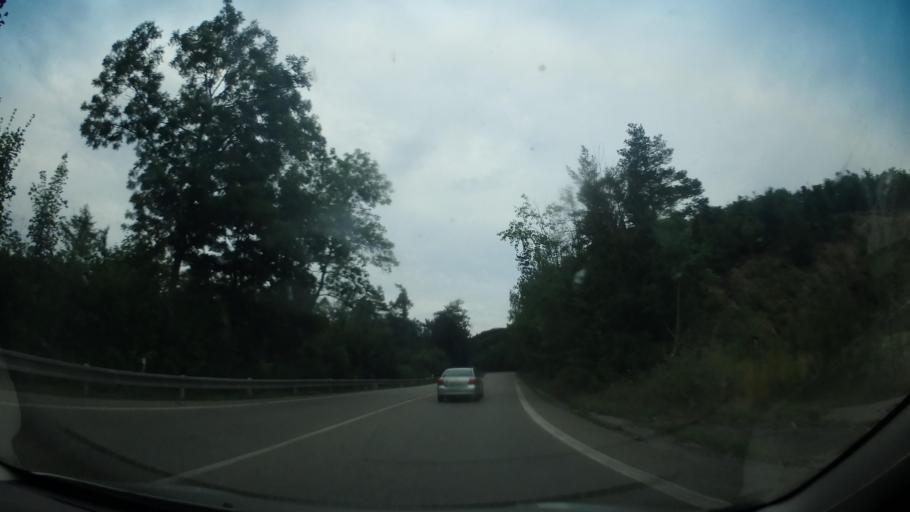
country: CZ
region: South Moravian
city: Troubsko
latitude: 49.1970
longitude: 16.5246
